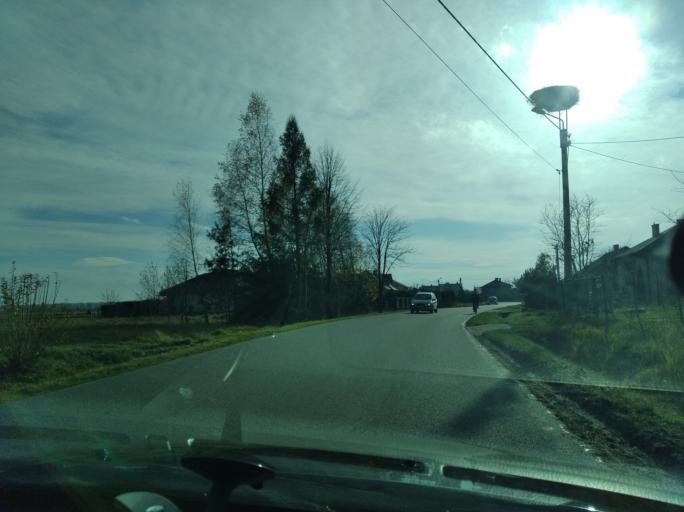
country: PL
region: Subcarpathian Voivodeship
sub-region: Powiat ropczycko-sedziszowski
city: Sedziszow Malopolski
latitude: 50.0816
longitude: 21.7507
